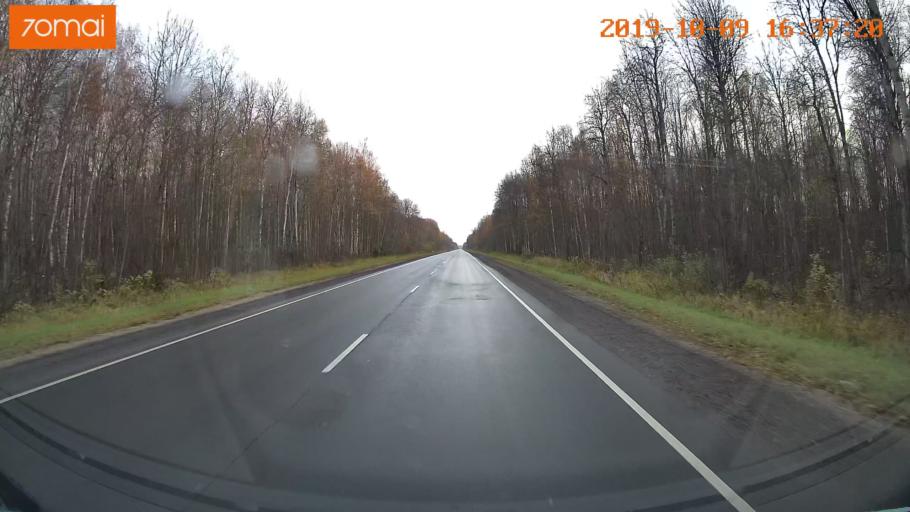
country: RU
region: Kostroma
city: Volgorechensk
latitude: 57.5284
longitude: 41.0234
